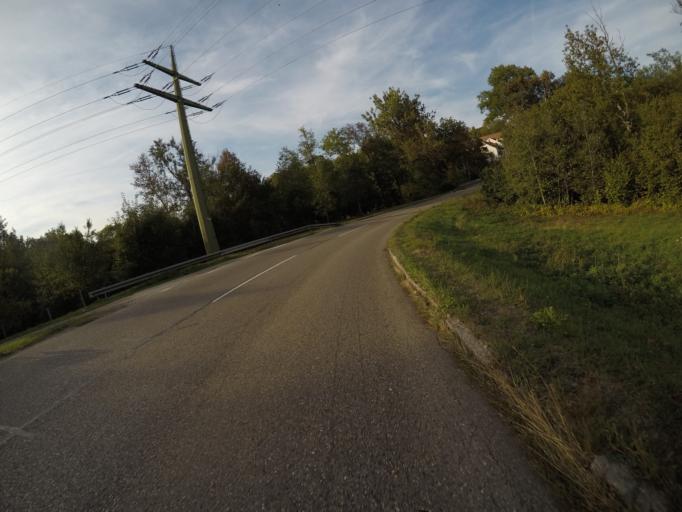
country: DE
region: Baden-Wuerttemberg
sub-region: Regierungsbezirk Stuttgart
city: Neuhausen auf den Fildern
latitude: 48.7024
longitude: 9.2868
